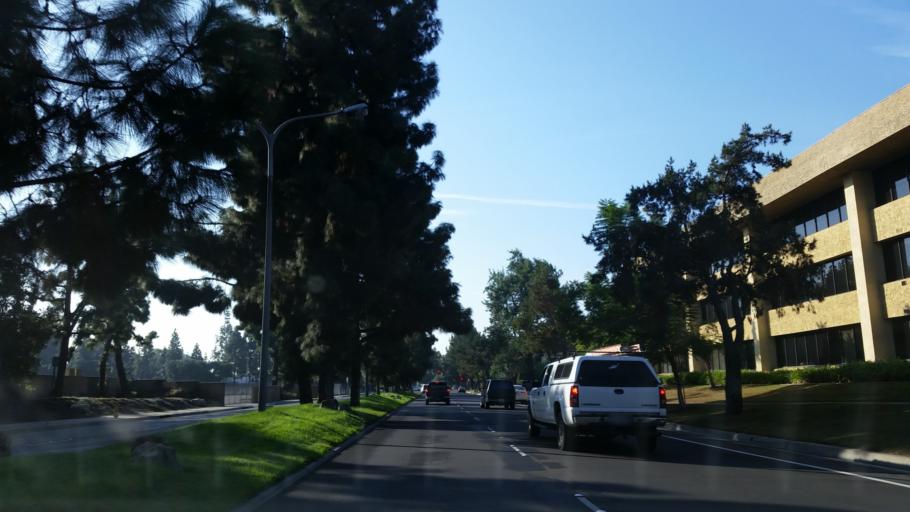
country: US
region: California
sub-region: Los Angeles County
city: Bellflower
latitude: 33.8752
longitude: -118.0998
